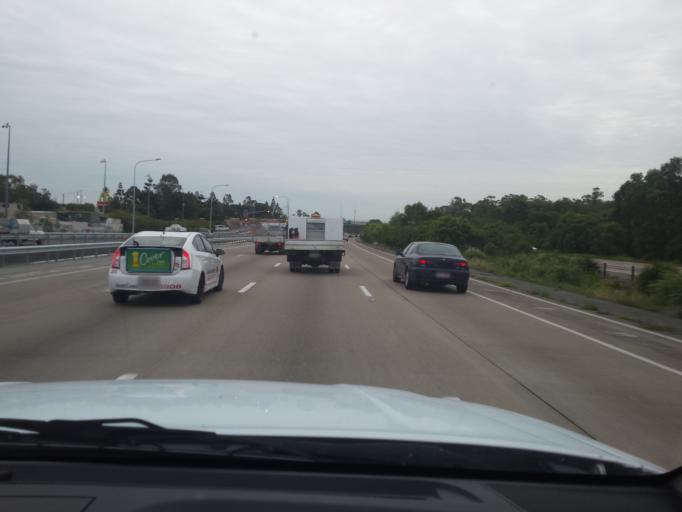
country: AU
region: Queensland
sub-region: Gold Coast
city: Oxenford
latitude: -27.8611
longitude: 153.3102
